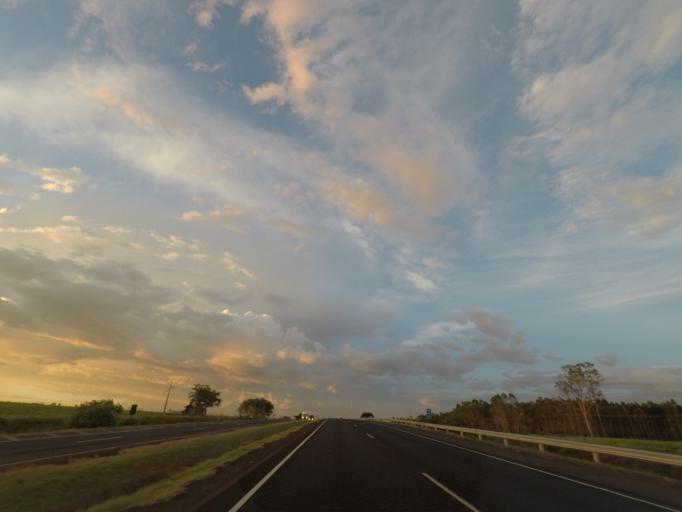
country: BR
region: Minas Gerais
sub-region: Uberaba
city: Uberaba
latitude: -19.6418
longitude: -48.0093
